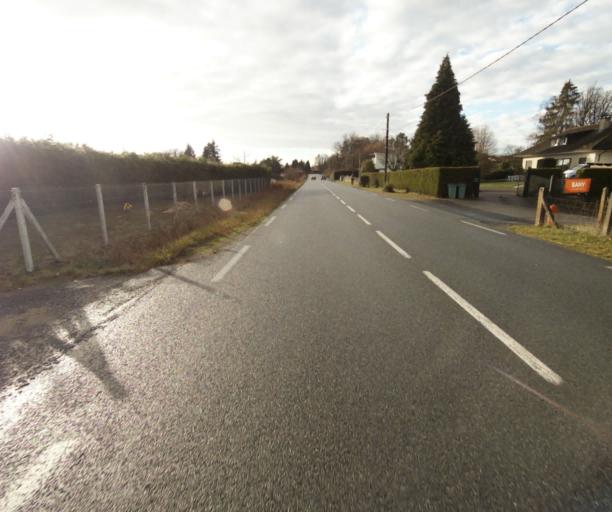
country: FR
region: Limousin
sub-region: Departement de la Correze
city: Saint-Mexant
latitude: 45.2593
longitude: 1.6353
